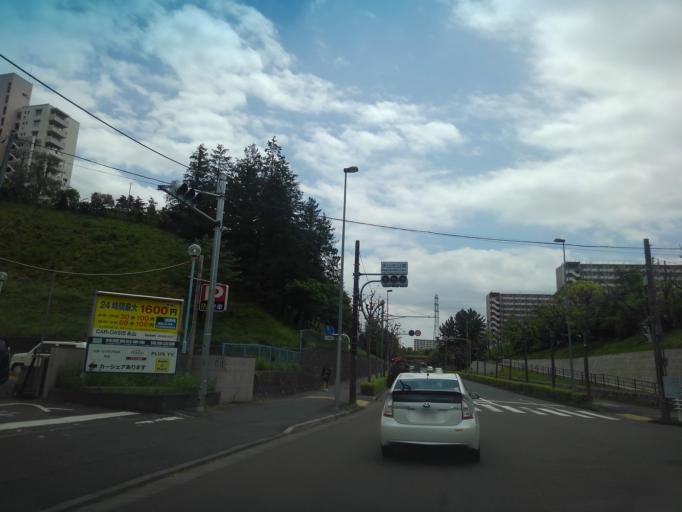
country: JP
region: Tokyo
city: Hino
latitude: 35.6282
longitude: 139.4492
